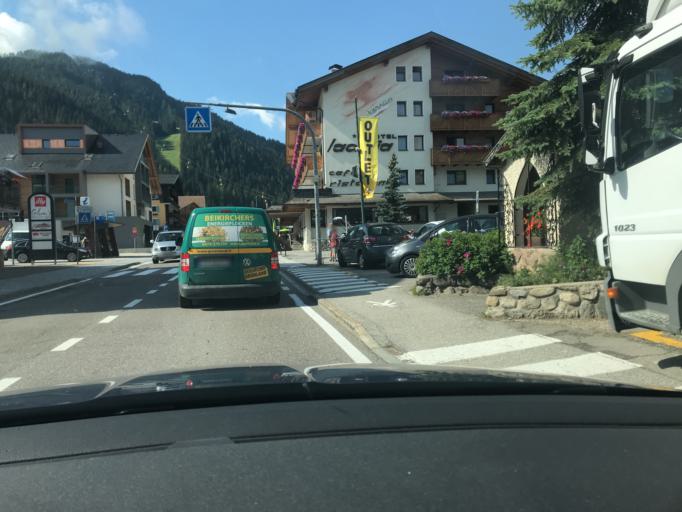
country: IT
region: Trentino-Alto Adige
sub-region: Bolzano
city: Badia
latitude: 46.5840
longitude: 11.9040
